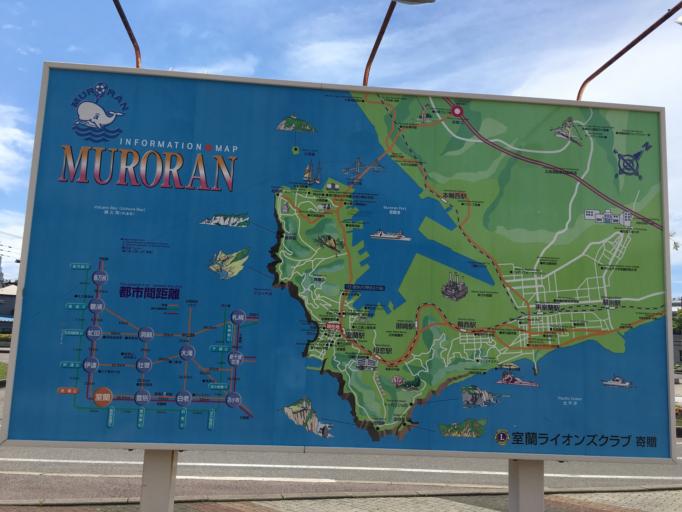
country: JP
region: Hokkaido
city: Muroran
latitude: 42.3181
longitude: 140.9741
